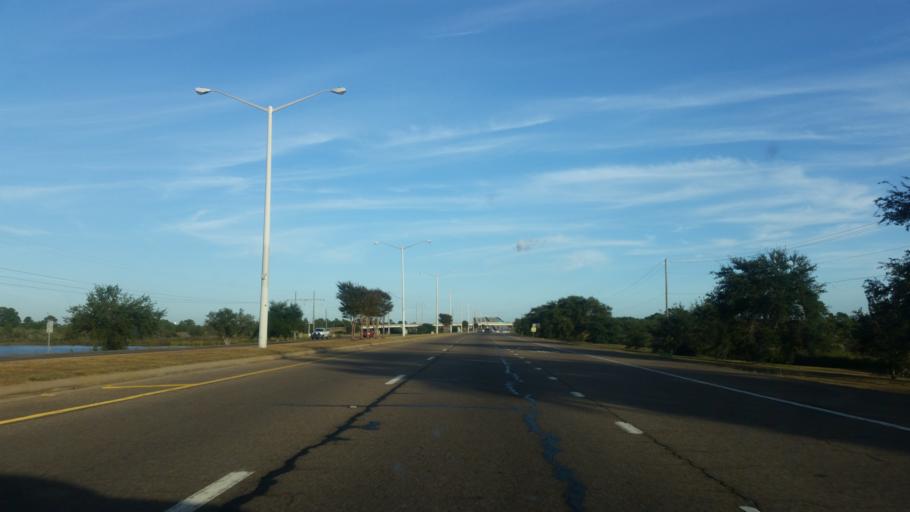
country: US
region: Mississippi
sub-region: Jackson County
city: Pascagoula
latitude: 30.3756
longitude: -88.5770
